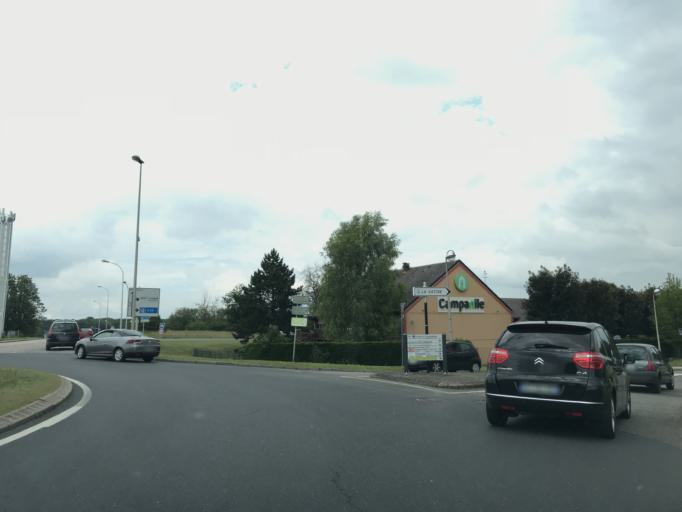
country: FR
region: Haute-Normandie
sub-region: Departement de la Seine-Maritime
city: Mont-Saint-Aignan
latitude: 49.4766
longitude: 1.0930
